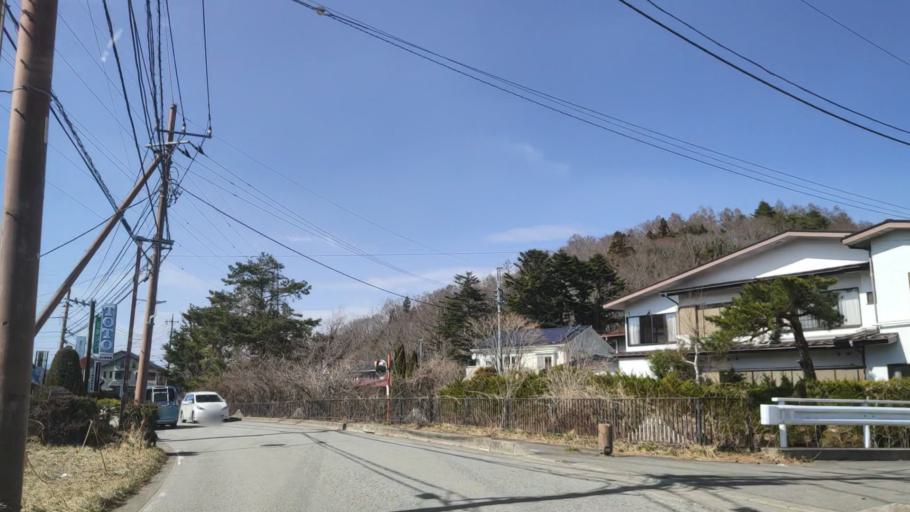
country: JP
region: Shizuoka
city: Gotemba
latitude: 35.4306
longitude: 138.8510
